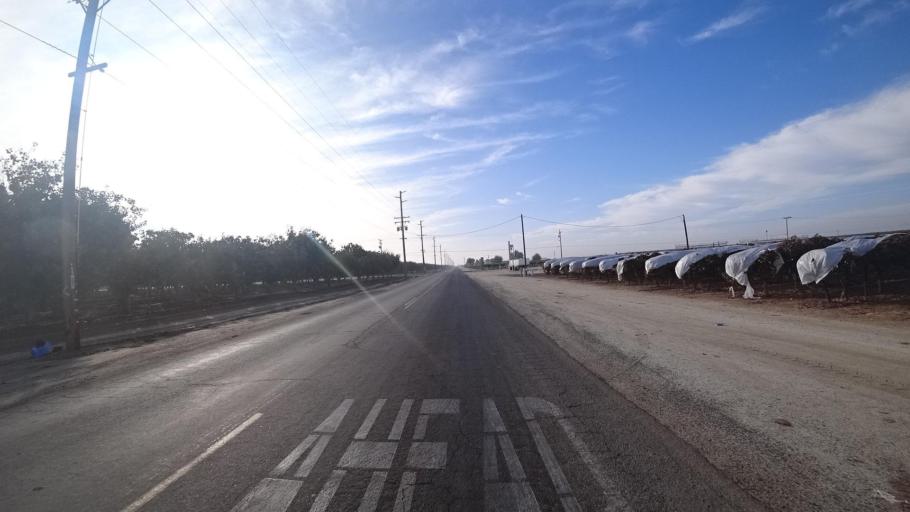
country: US
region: California
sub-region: Kern County
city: McFarland
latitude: 35.7187
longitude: -119.2046
